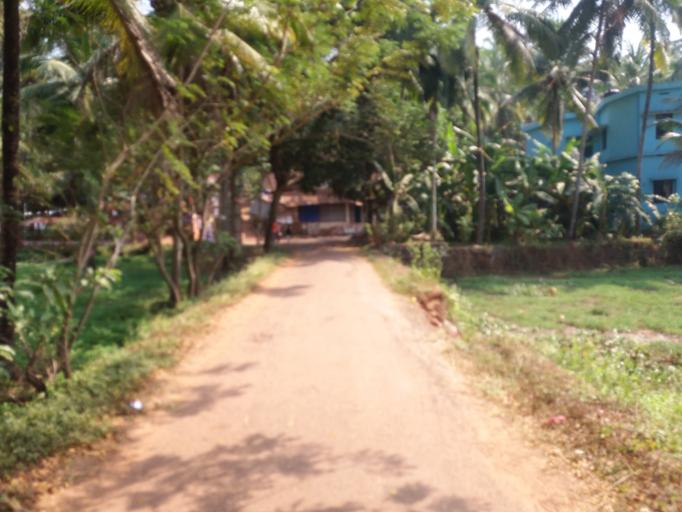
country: IN
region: Kerala
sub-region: Kozhikode
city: Kunnamangalam
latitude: 11.3004
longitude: 75.8214
